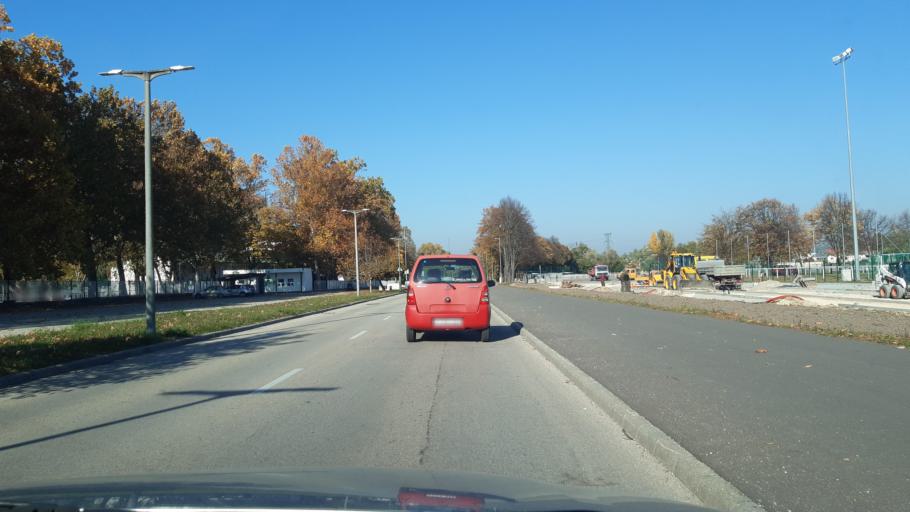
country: HU
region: Veszprem
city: Ajka
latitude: 47.1095
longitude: 17.5510
